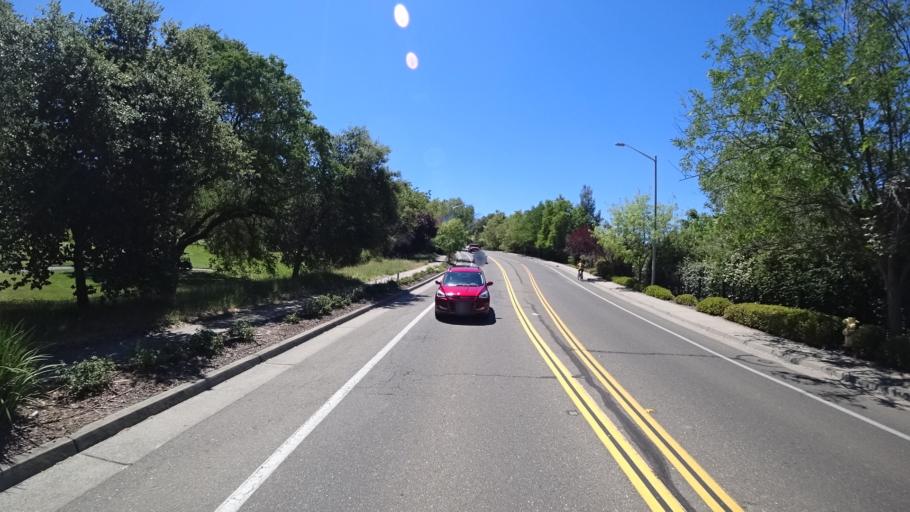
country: US
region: California
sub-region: Placer County
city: Rocklin
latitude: 38.8217
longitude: -121.2427
